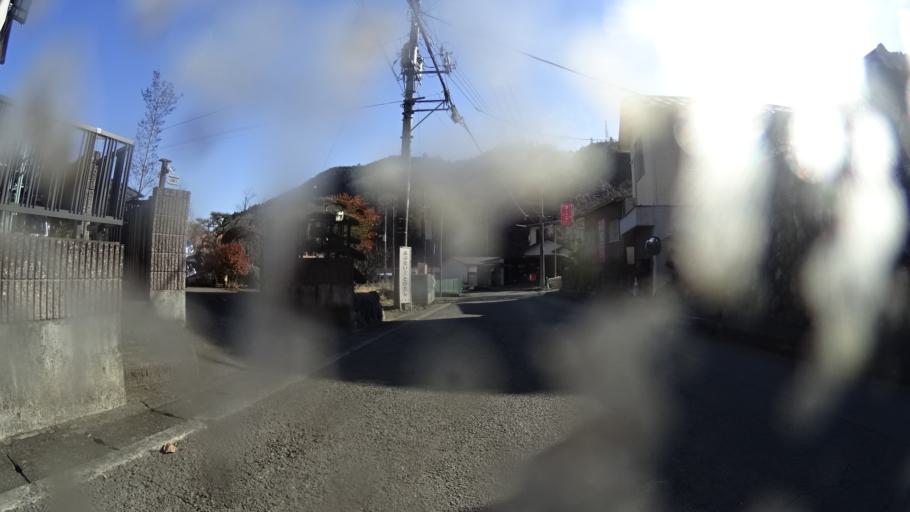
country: JP
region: Yamanashi
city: Uenohara
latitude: 35.6221
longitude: 139.1532
